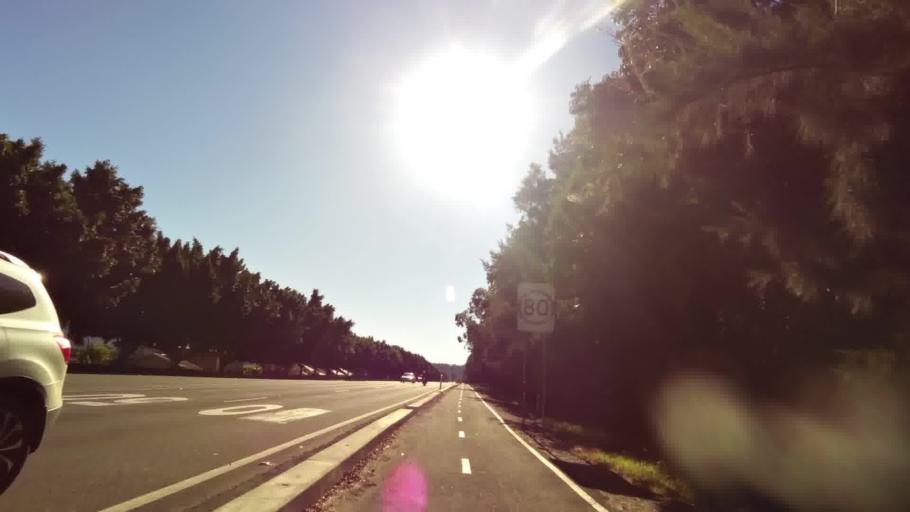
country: AU
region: New South Wales
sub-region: Wollongong
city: Koonawarra
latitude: -34.4886
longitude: 150.7978
